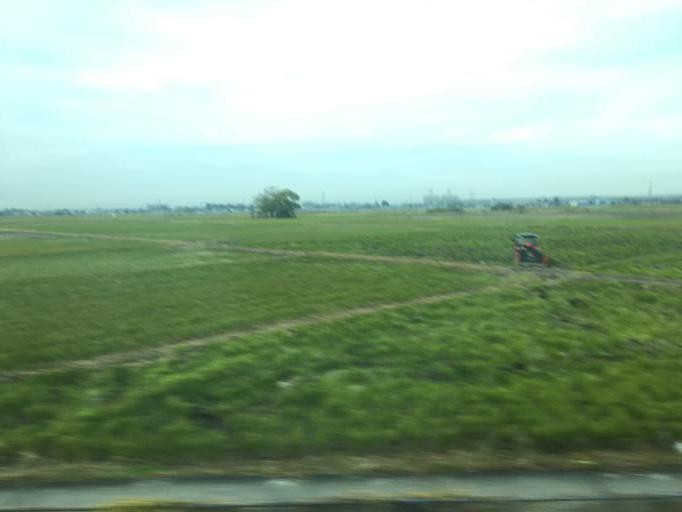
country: JP
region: Saitama
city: Kamifukuoka
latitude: 35.9038
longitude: 139.5320
